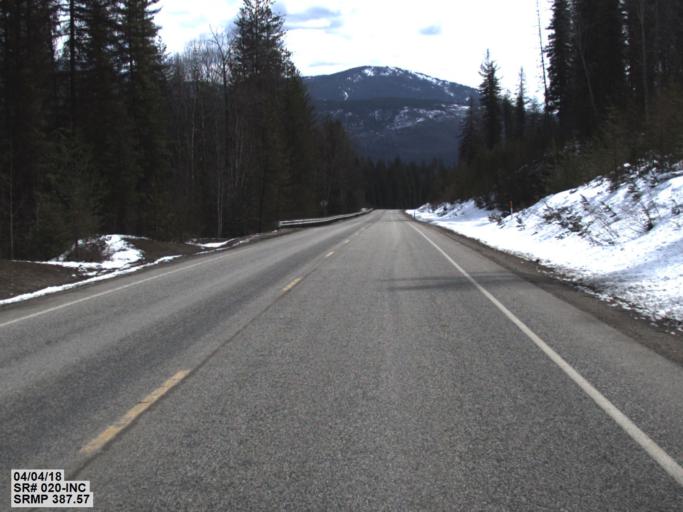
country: CA
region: British Columbia
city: Fruitvale
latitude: 48.6814
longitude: -117.4449
